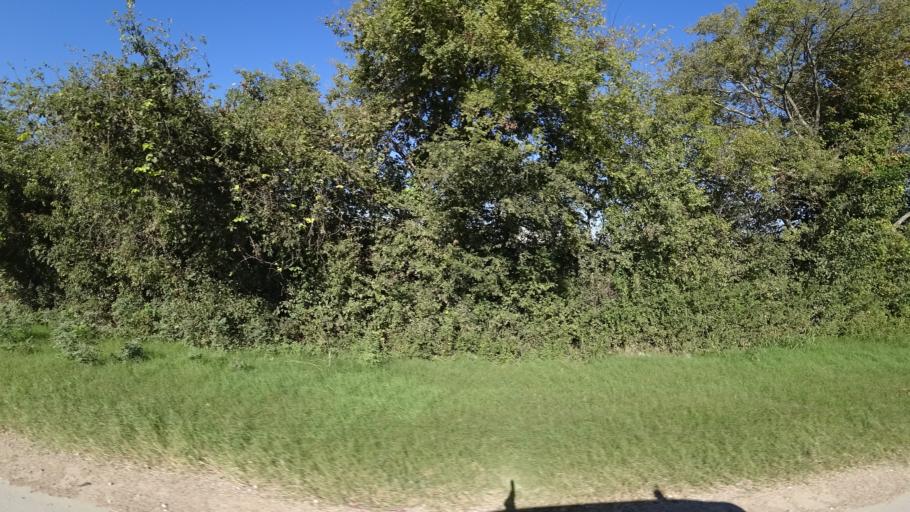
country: US
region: Texas
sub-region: Travis County
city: Hornsby Bend
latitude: 30.2404
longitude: -97.6224
